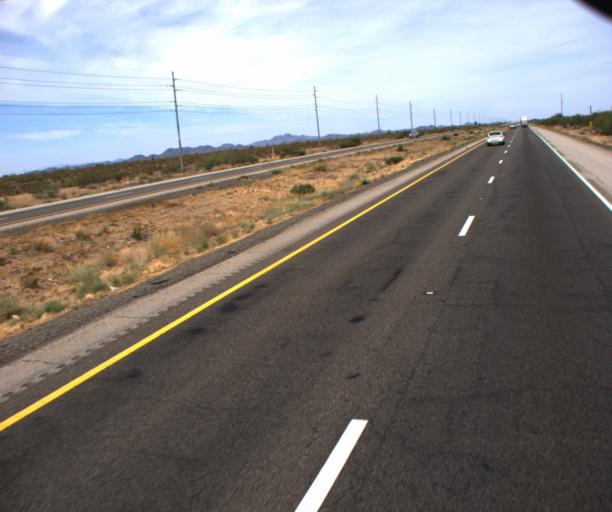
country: US
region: Arizona
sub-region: Maricopa County
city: Wickenburg
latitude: 33.8007
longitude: -112.5577
